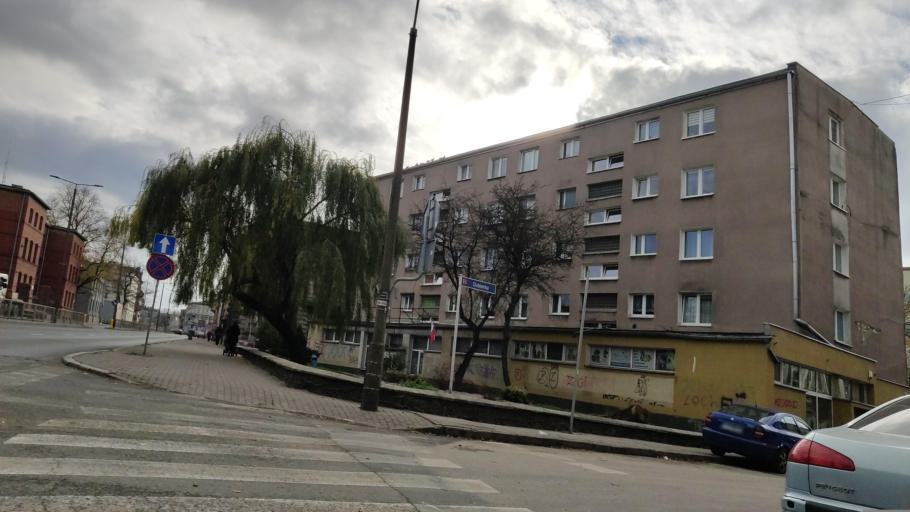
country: PL
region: Kujawsko-Pomorskie
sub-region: Powiat inowroclawski
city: Inowroclaw
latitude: 52.8037
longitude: 18.2495
